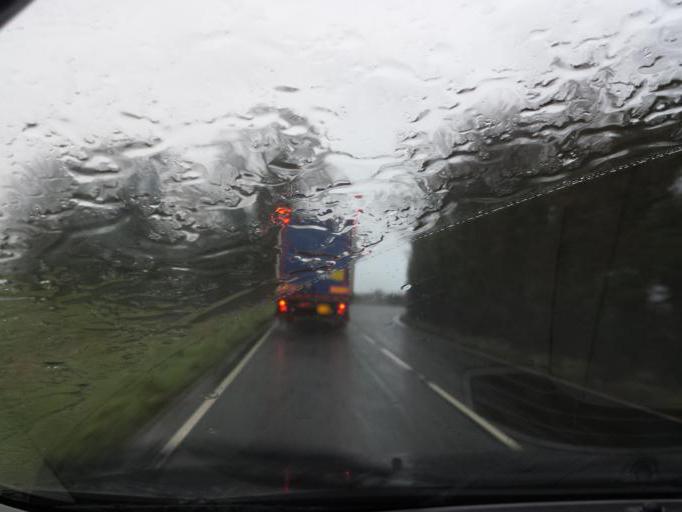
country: GB
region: Northern Ireland
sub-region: Antrim Borough
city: Antrim
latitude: 54.6658
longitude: -6.2200
